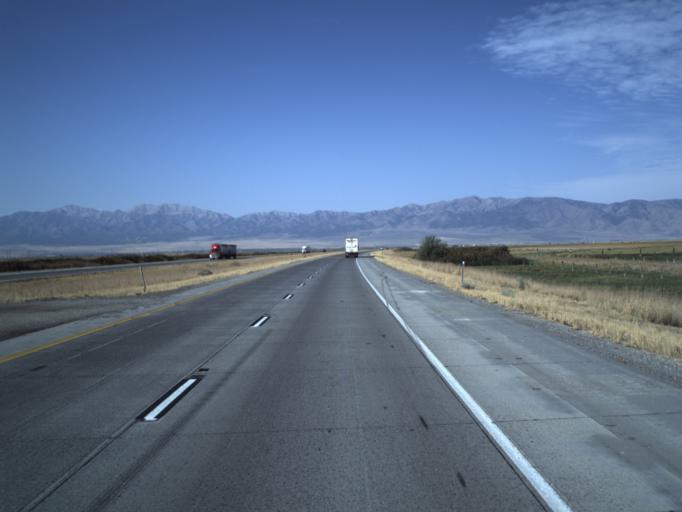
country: US
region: Utah
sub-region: Tooele County
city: Stansbury park
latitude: 40.6684
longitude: -112.3033
